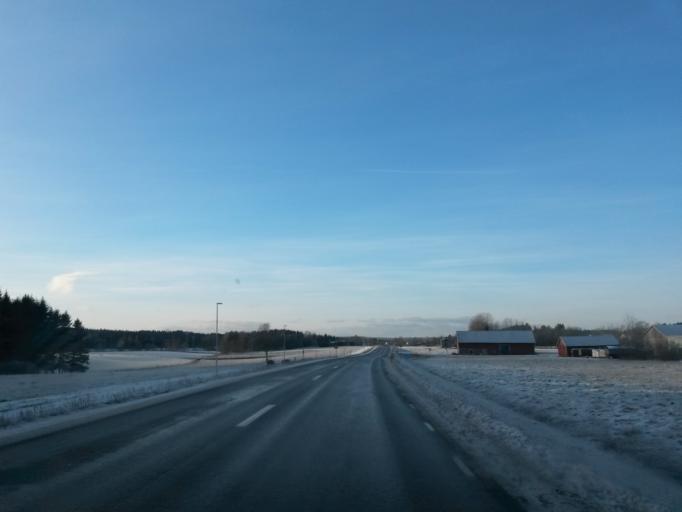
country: SE
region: Vaestra Goetaland
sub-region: Alingsas Kommun
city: Sollebrunn
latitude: 58.1086
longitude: 12.6009
